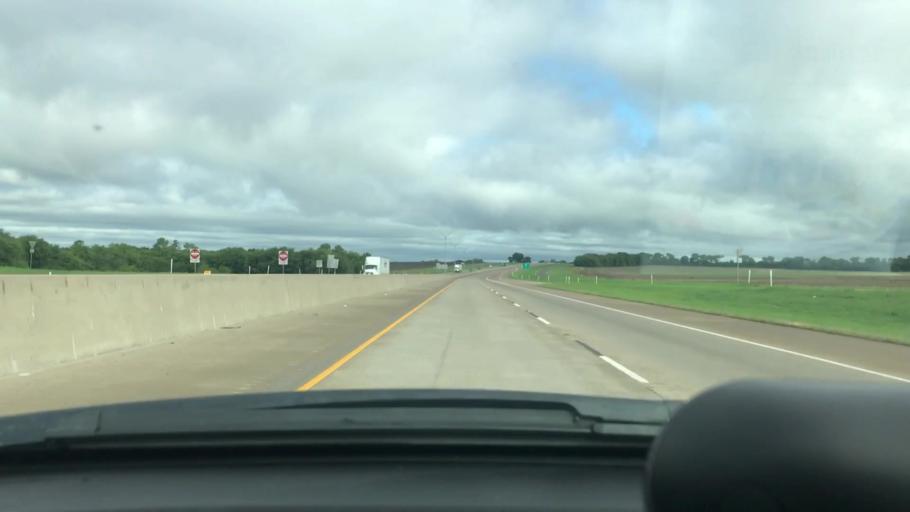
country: US
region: Texas
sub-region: Grayson County
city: Howe
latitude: 33.4706
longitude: -96.6157
